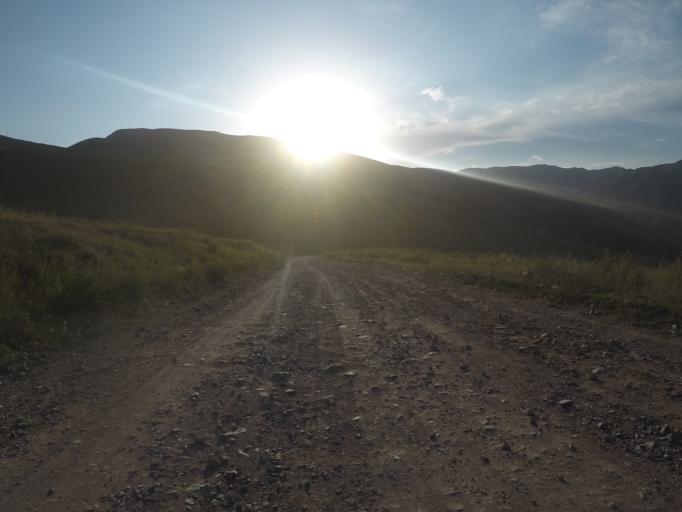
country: KG
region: Chuy
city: Bishkek
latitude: 42.6562
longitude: 74.6535
